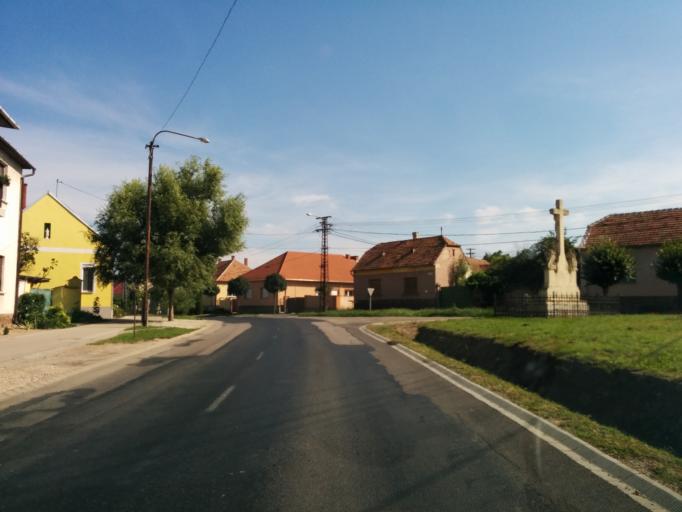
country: HU
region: Gyor-Moson-Sopron
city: Fertoszentmiklos
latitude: 47.5826
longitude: 16.8794
